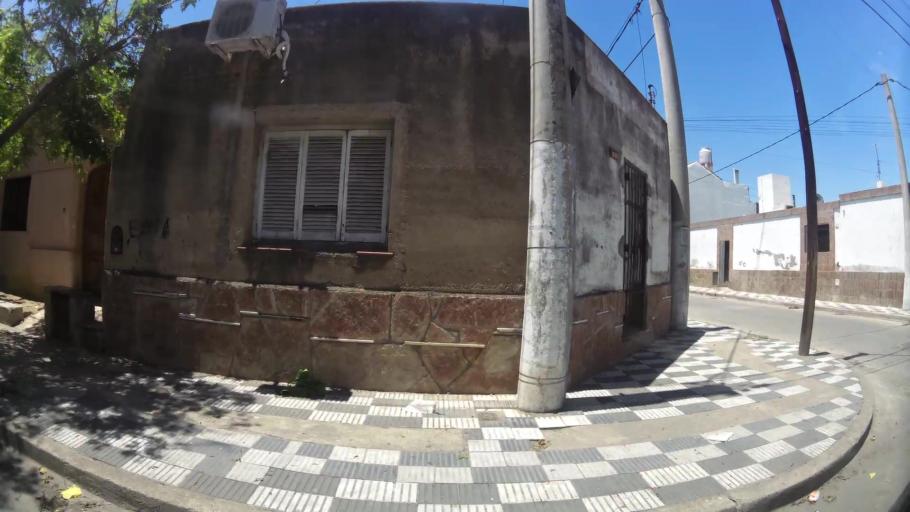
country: AR
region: Cordoba
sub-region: Departamento de Capital
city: Cordoba
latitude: -31.3928
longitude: -64.2088
